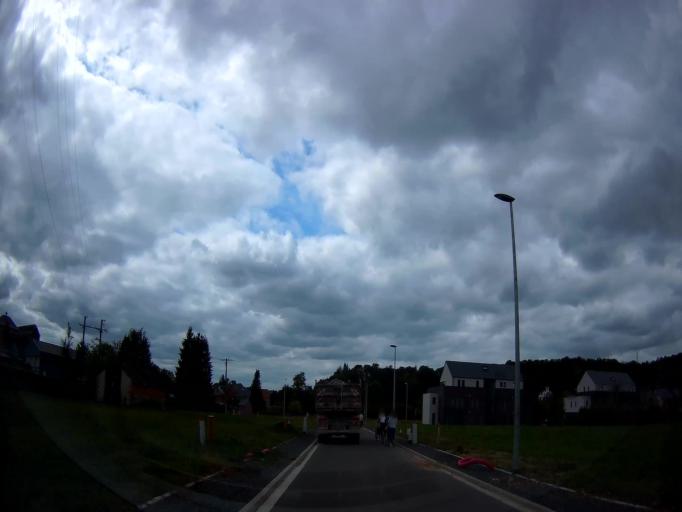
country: BE
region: Wallonia
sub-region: Province de Namur
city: Rochefort
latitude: 50.1638
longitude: 5.2241
